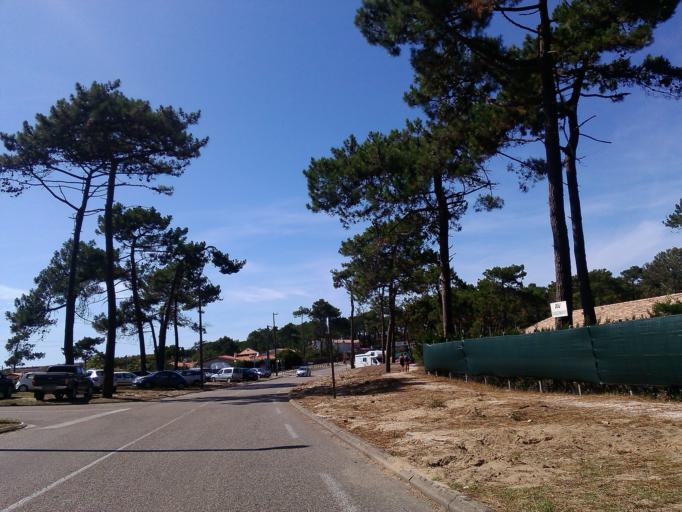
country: FR
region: Aquitaine
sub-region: Departement de la Gironde
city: Lacanau
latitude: 45.0069
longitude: -1.1927
